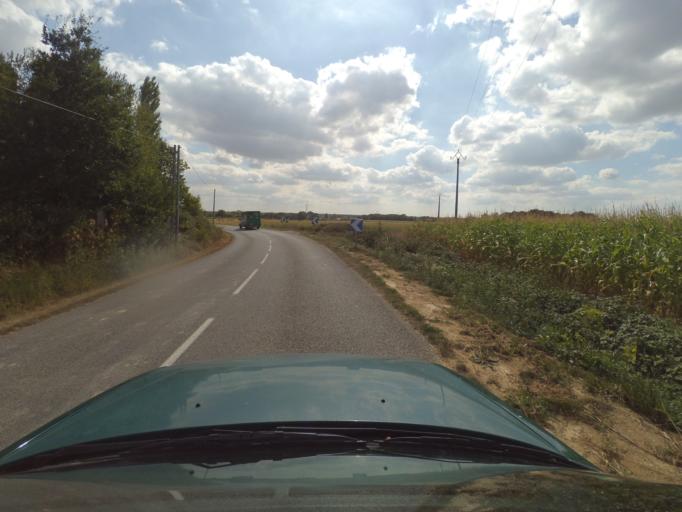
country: FR
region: Pays de la Loire
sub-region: Departement de la Loire-Atlantique
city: La Planche
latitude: 47.0300
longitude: -1.4216
